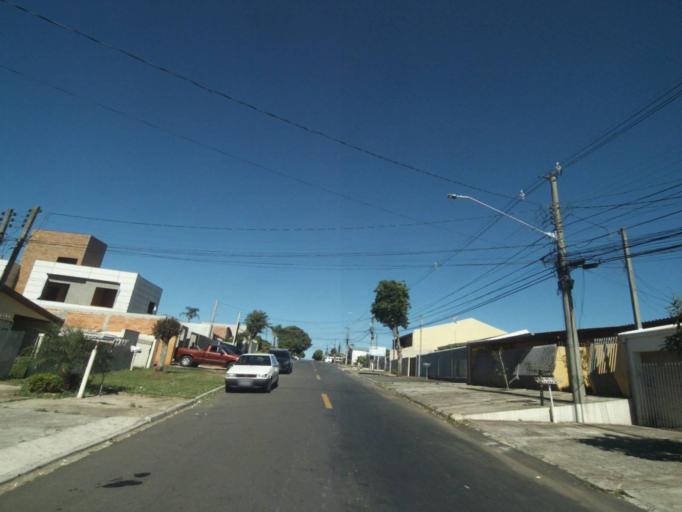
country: BR
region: Parana
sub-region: Curitiba
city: Curitiba
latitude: -25.4551
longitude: -49.3477
